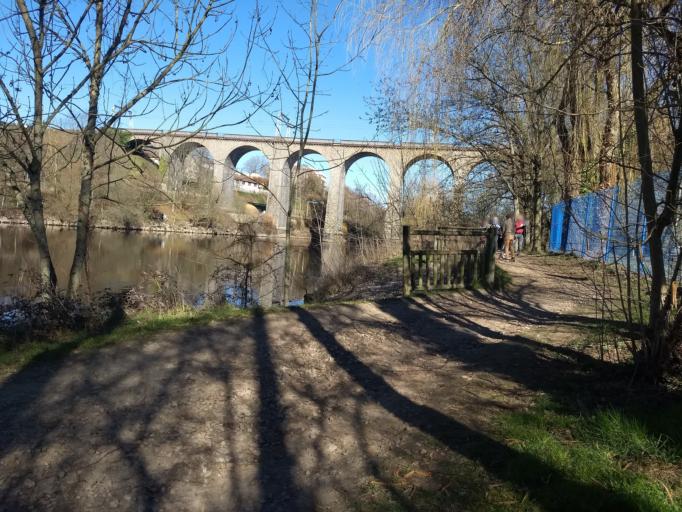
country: FR
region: Limousin
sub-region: Departement de la Haute-Vienne
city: Limoges
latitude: 45.8182
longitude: 1.2583
